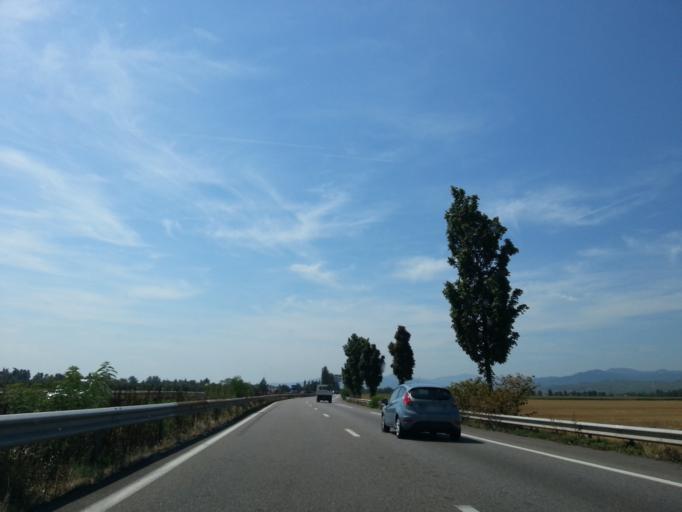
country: FR
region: Alsace
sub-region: Departement du Haut-Rhin
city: Ostheim
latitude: 48.1744
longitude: 7.3781
